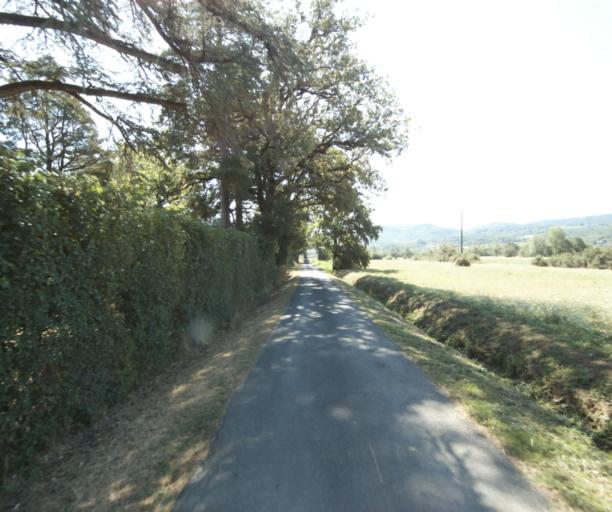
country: FR
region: Midi-Pyrenees
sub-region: Departement de la Haute-Garonne
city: Revel
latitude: 43.4584
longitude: 2.0313
